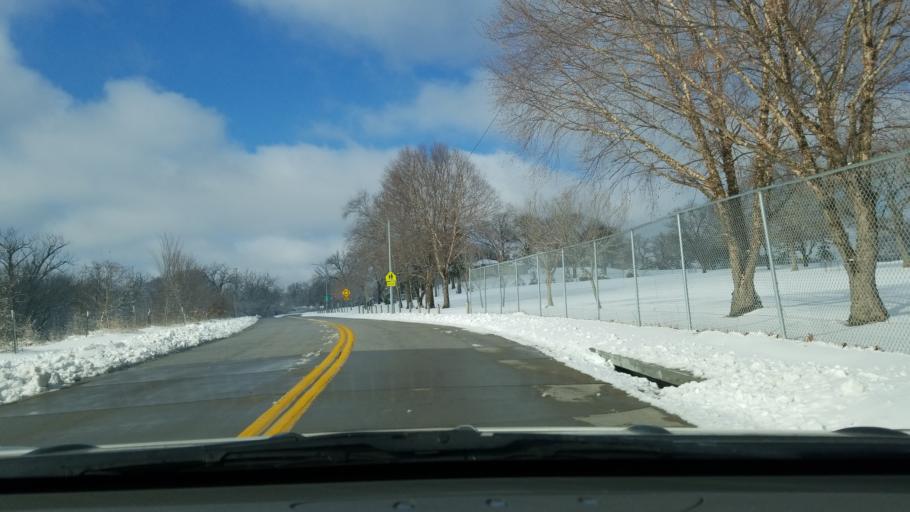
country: US
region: Nebraska
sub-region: Douglas County
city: Omaha
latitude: 41.2194
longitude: -95.9364
